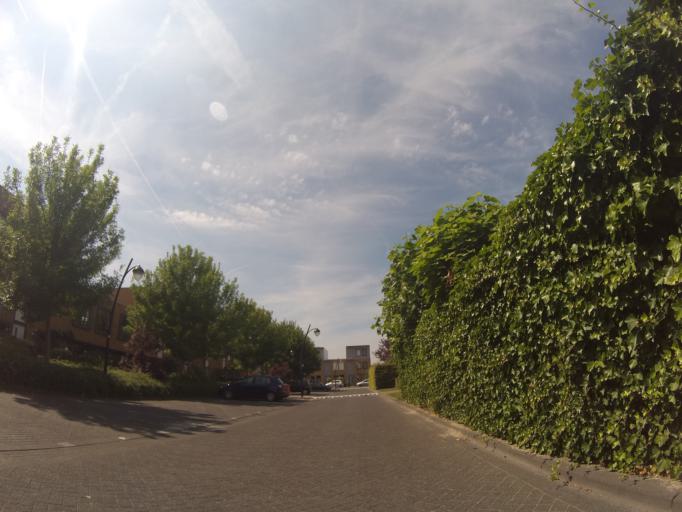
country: NL
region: Utrecht
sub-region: Gemeente Amersfoort
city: Hoogland
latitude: 52.1983
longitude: 5.4242
